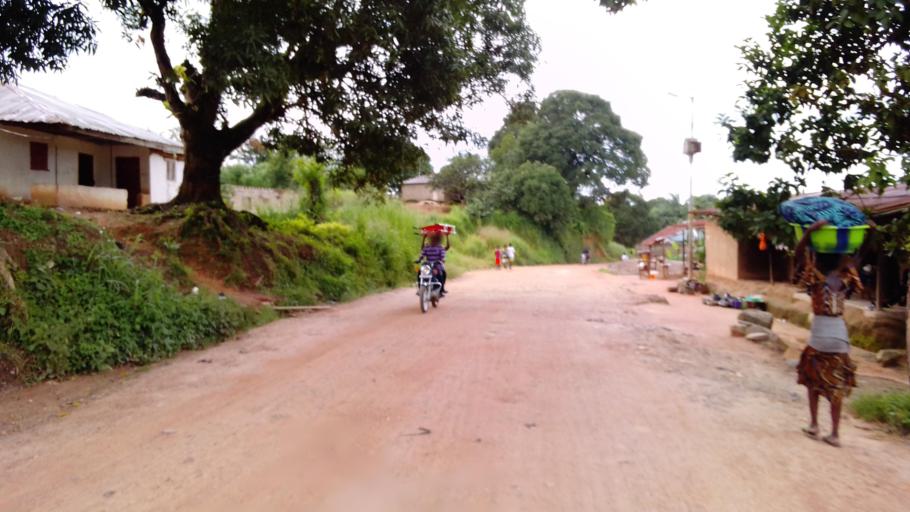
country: SL
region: Eastern Province
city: Koidu
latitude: 8.6577
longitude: -10.9761
